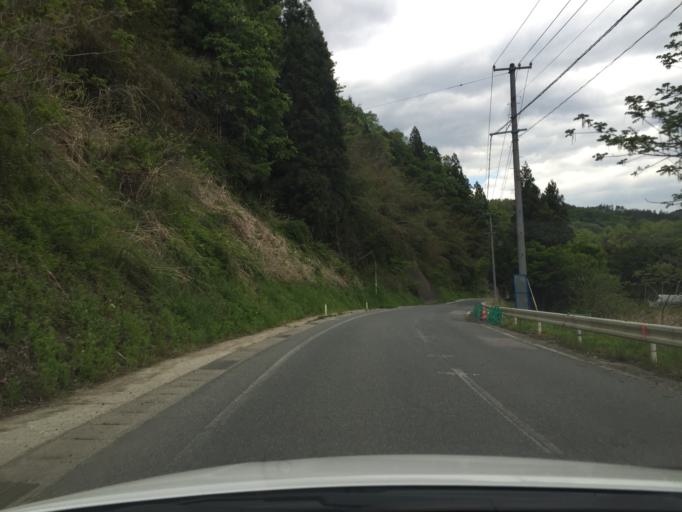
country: JP
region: Fukushima
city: Yanagawamachi-saiwaicho
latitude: 37.7559
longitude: 140.6440
